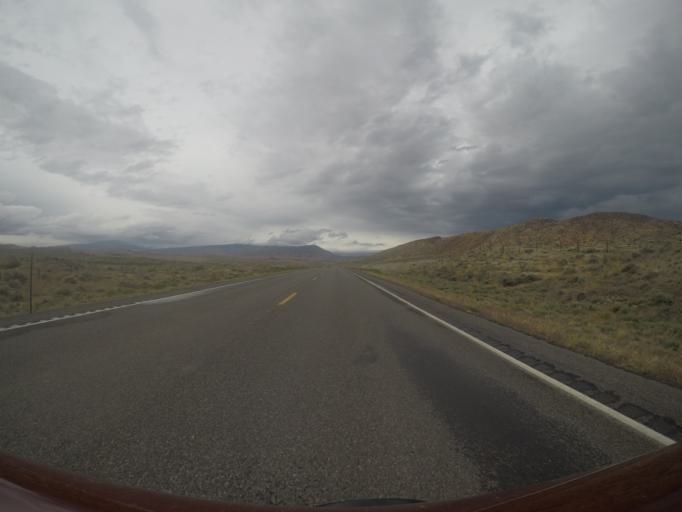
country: US
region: Wyoming
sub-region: Big Horn County
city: Lovell
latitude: 44.9314
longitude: -108.2982
